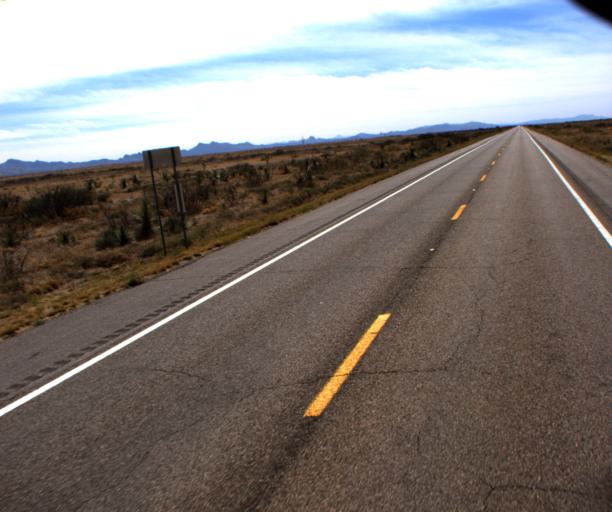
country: US
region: Arizona
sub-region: Cochise County
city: Pirtleville
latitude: 31.5249
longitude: -109.6484
